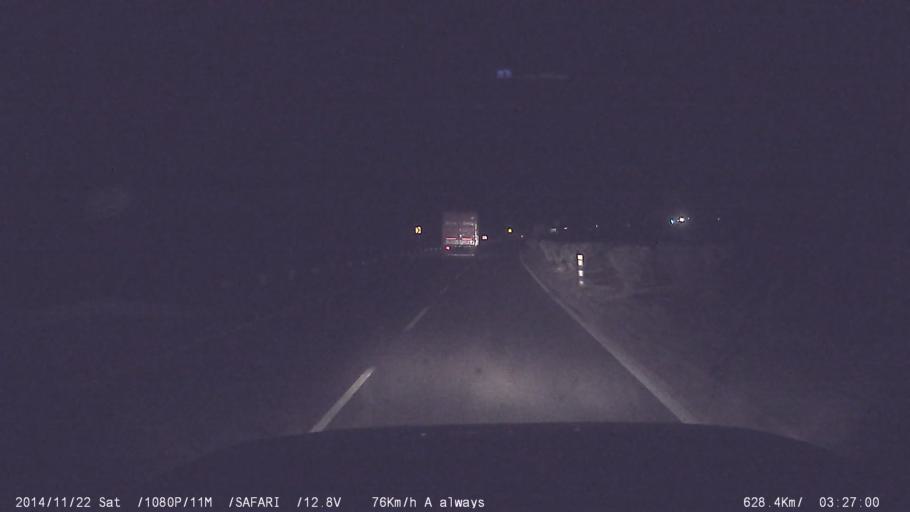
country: IN
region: Tamil Nadu
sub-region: Salem
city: Konganapuram
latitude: 11.5325
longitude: 77.9557
